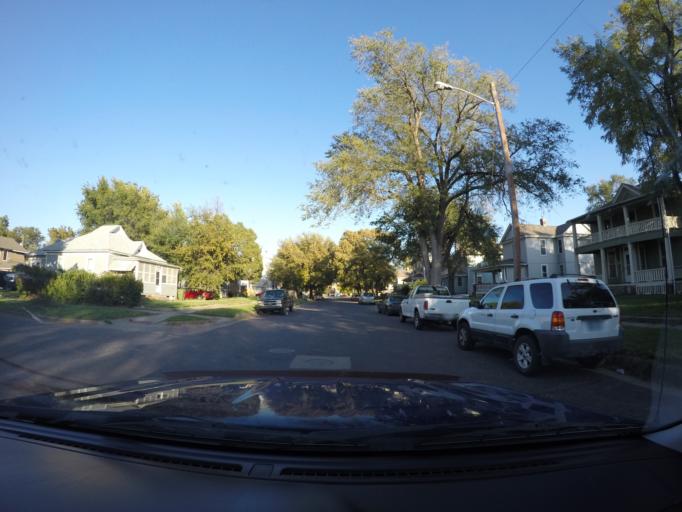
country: US
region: Kansas
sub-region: Saline County
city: Salina
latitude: 38.8417
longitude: -97.6148
